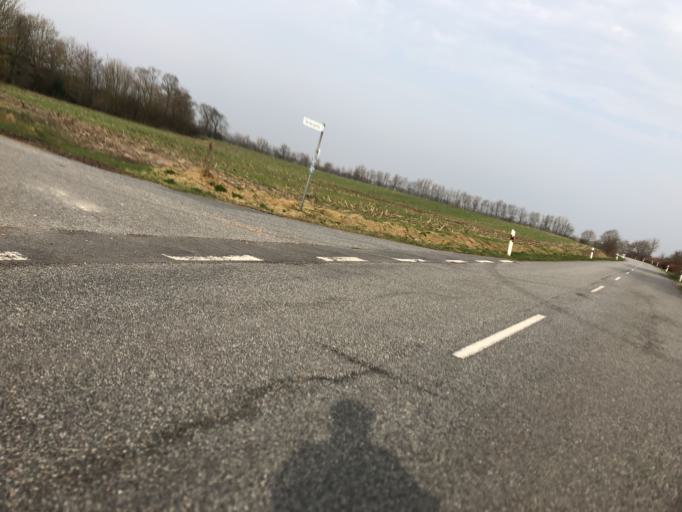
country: DE
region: Schleswig-Holstein
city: Sankelmark
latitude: 54.7056
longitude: 9.3895
